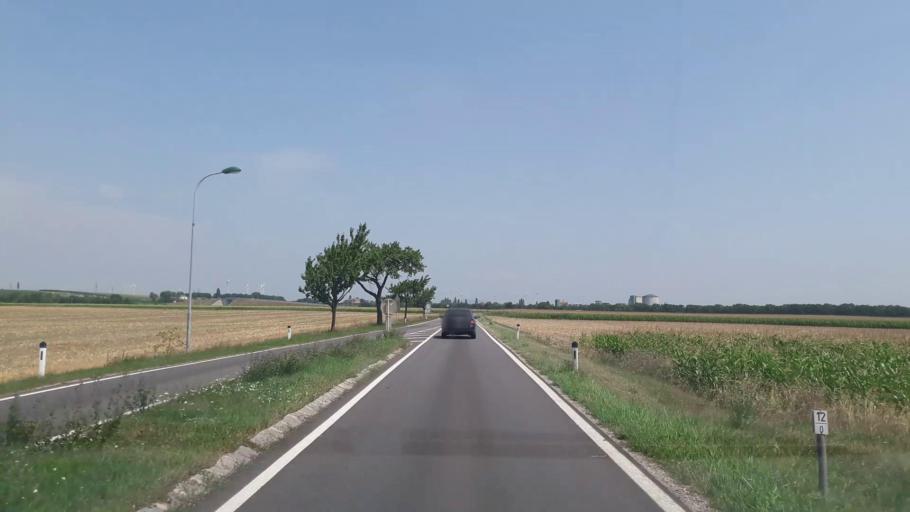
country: AT
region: Lower Austria
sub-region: Politischer Bezirk Bruck an der Leitha
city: Bruck an der Leitha
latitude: 48.0139
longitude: 16.7334
